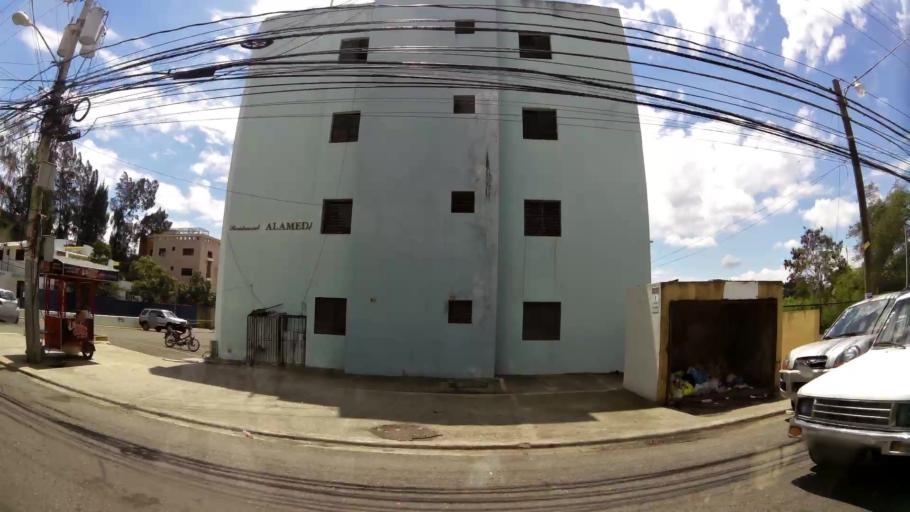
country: DO
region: Santiago
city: Santiago de los Caballeros
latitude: 19.4596
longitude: -70.6632
